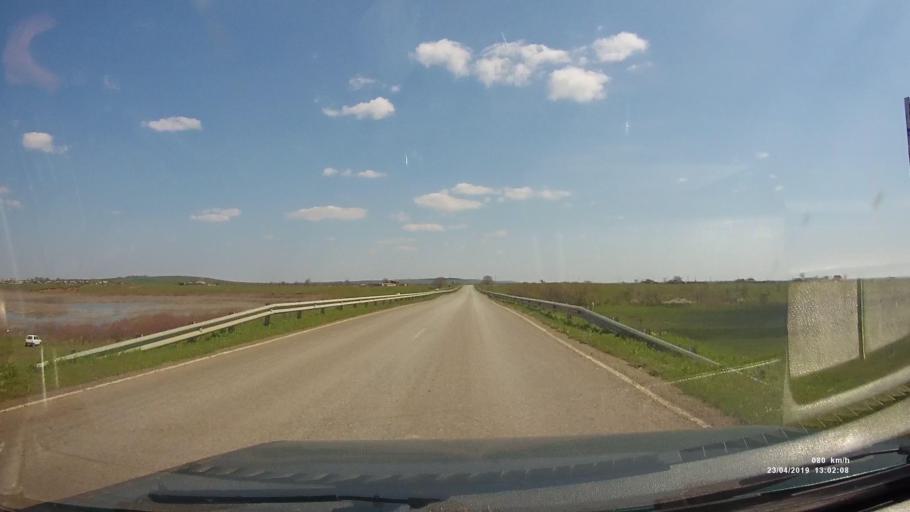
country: RU
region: Kalmykiya
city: Yashalta
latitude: 46.6017
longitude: 42.6649
